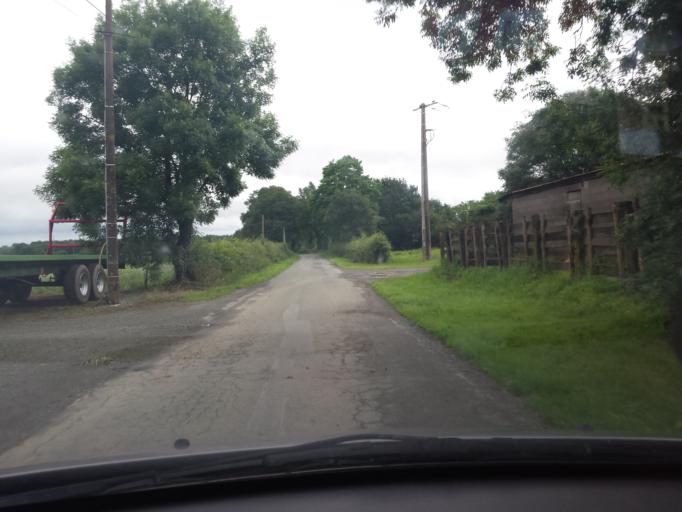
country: FR
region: Pays de la Loire
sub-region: Departement de la Vendee
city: Les Essarts
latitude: 46.7515
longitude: -1.2399
